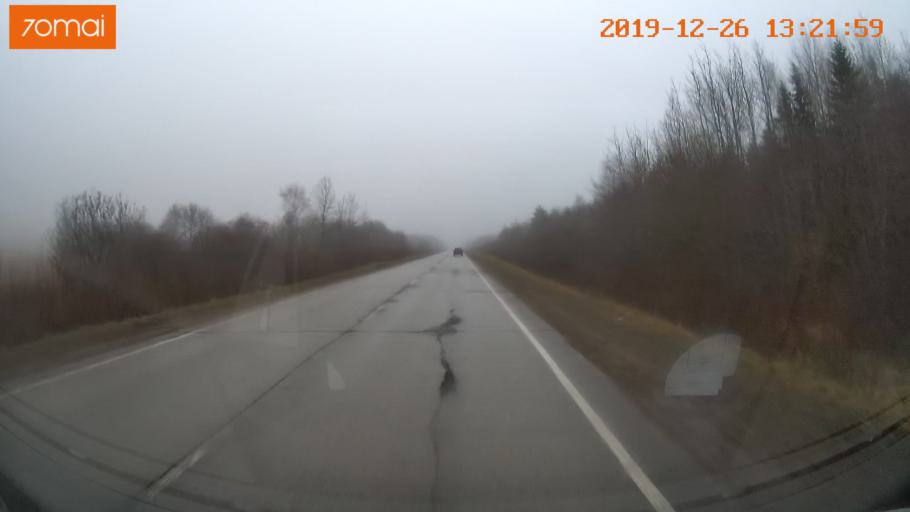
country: RU
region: Vologda
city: Cherepovets
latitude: 58.9070
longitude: 38.1659
